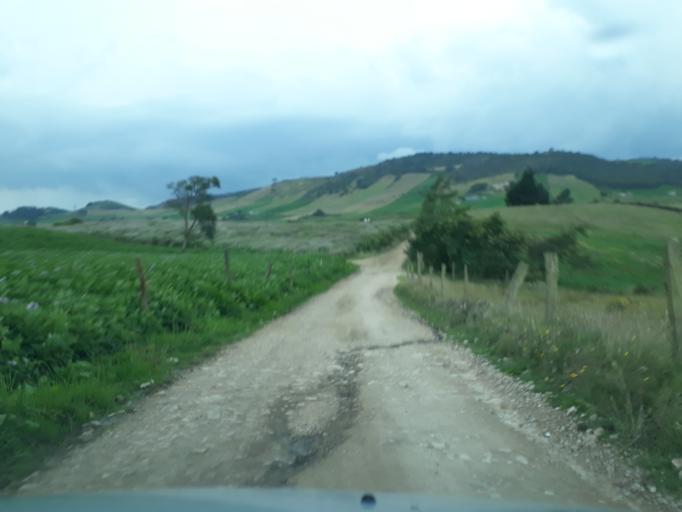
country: CO
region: Cundinamarca
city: Villapinzon
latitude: 5.2381
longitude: -73.6668
